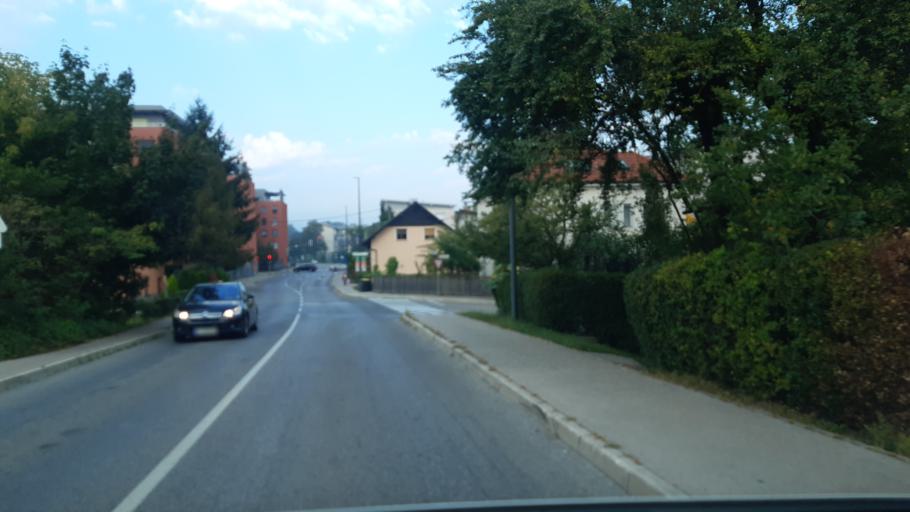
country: SI
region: Ljubljana
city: Ljubljana
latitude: 46.0421
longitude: 14.4747
